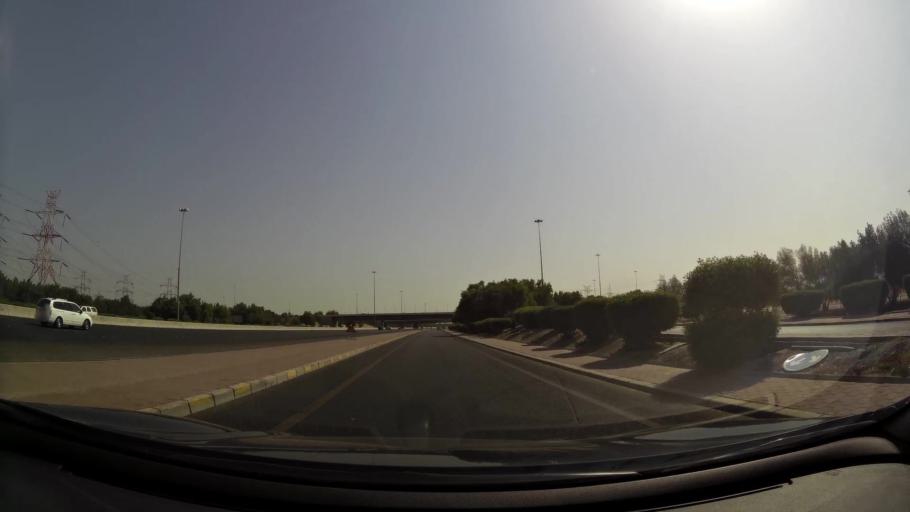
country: KW
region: Mubarak al Kabir
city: Sabah as Salim
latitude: 29.2684
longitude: 48.0405
